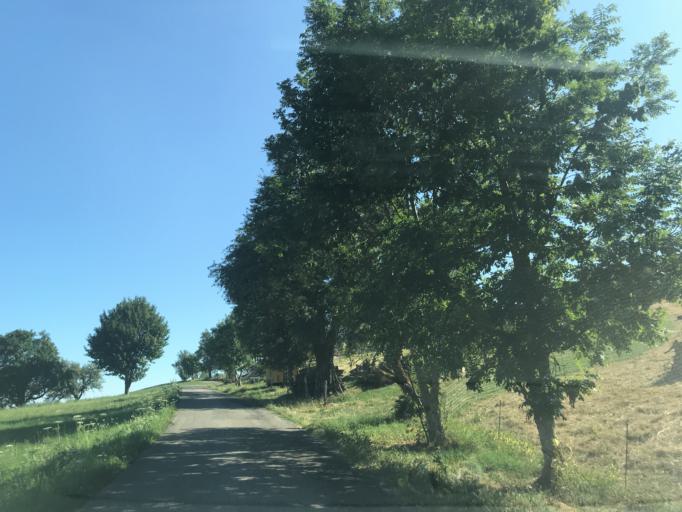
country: FR
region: Rhone-Alpes
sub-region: Departement de la Haute-Savoie
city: Thorens-Glieres
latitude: 45.9666
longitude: 6.2235
